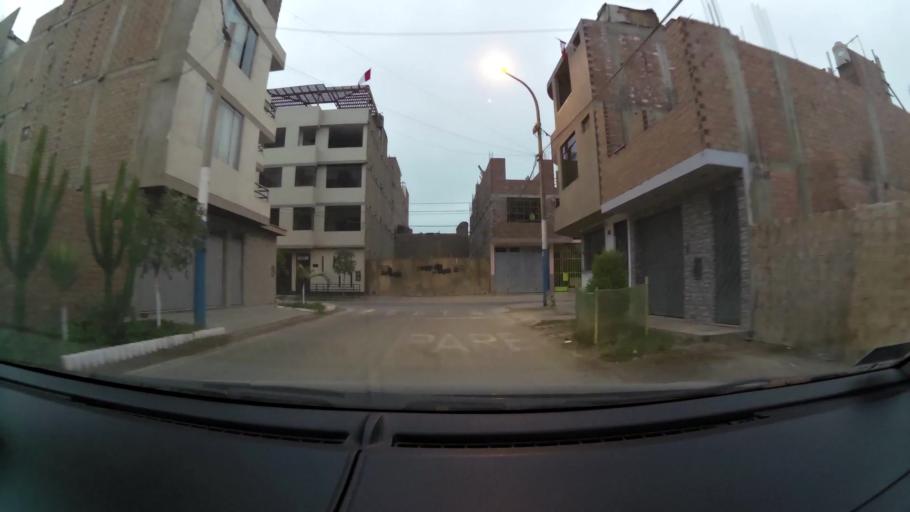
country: PE
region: Lima
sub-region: Lima
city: Independencia
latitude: -11.9801
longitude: -77.0972
